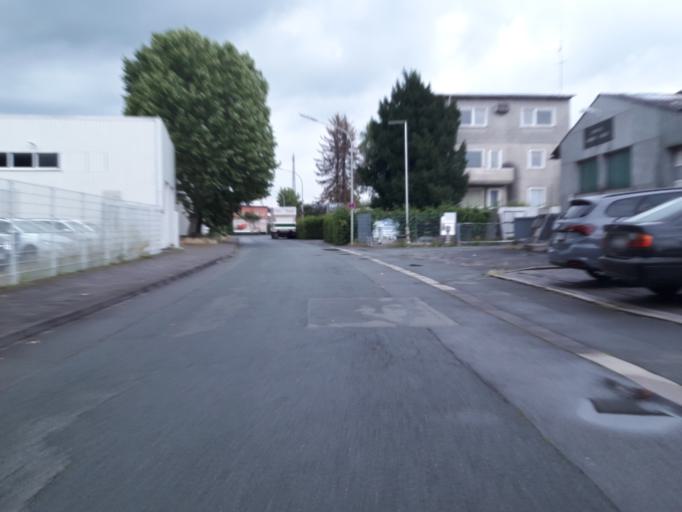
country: DE
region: North Rhine-Westphalia
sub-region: Regierungsbezirk Detmold
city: Paderborn
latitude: 51.7089
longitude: 8.7344
